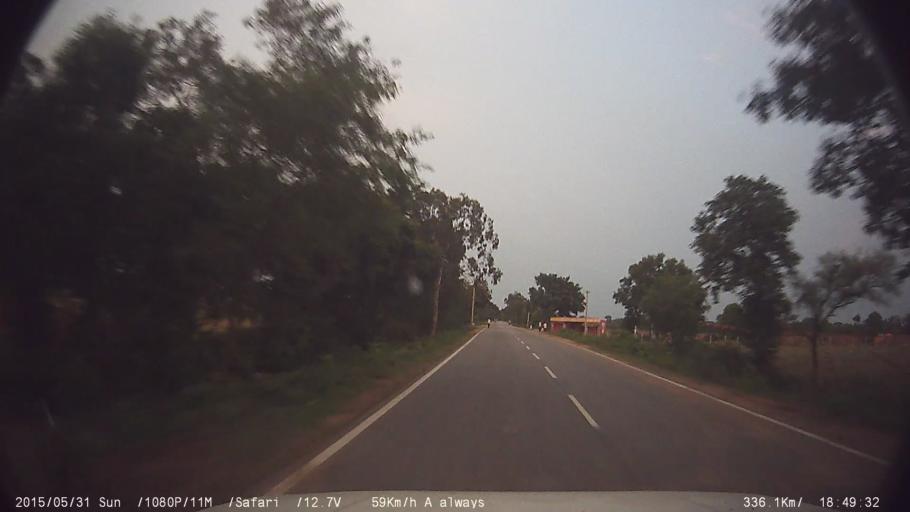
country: IN
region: Karnataka
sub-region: Mysore
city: Tirumakudal Narsipur
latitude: 12.1740
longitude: 76.8515
